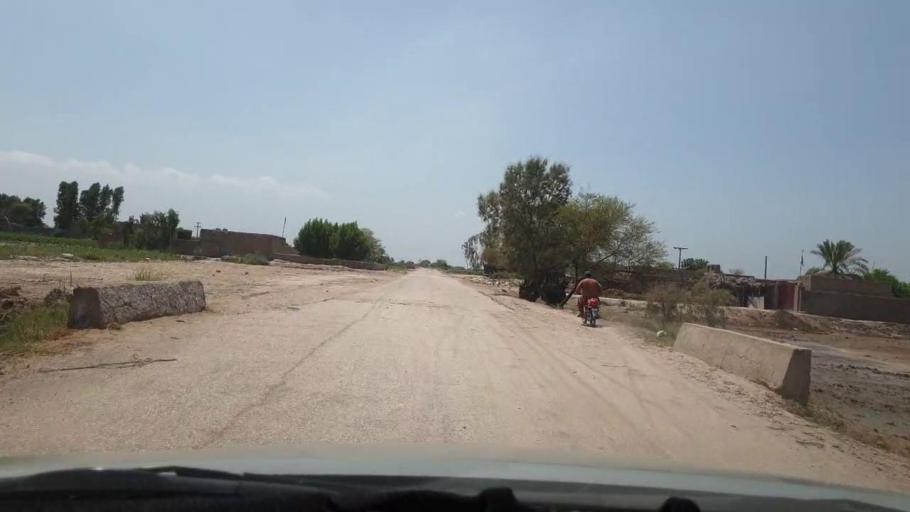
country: PK
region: Sindh
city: Pano Aqil
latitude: 27.6635
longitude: 69.1341
